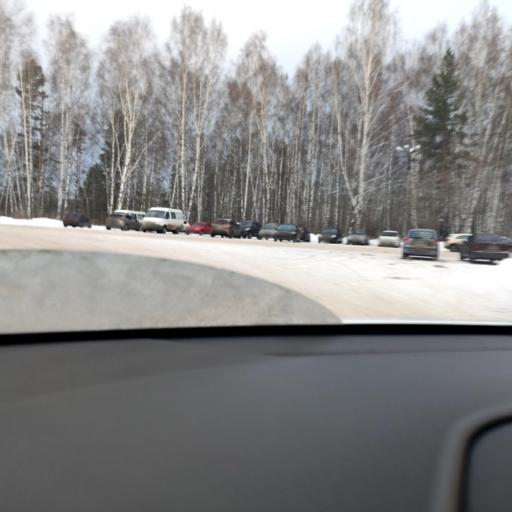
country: RU
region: Tatarstan
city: Osinovo
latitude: 55.8911
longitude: 48.8267
